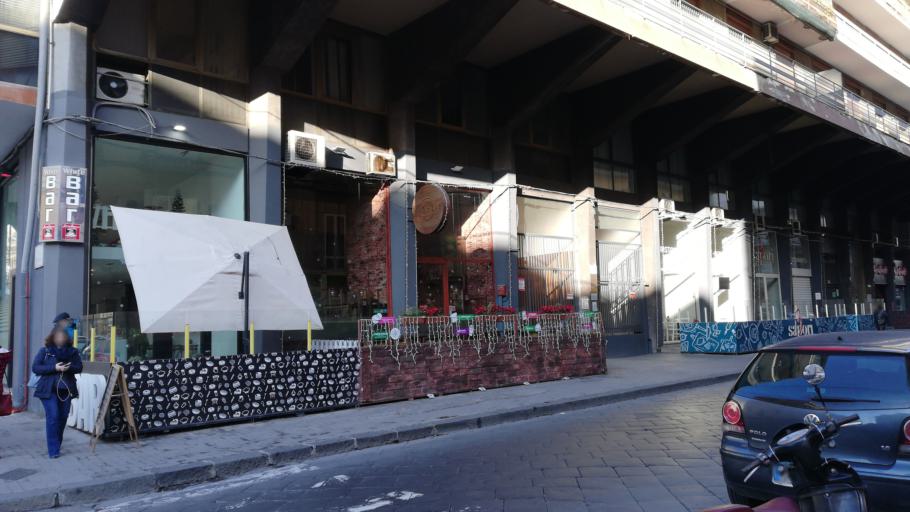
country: IT
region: Sicily
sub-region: Catania
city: Canalicchio
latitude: 37.5169
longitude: 15.0985
